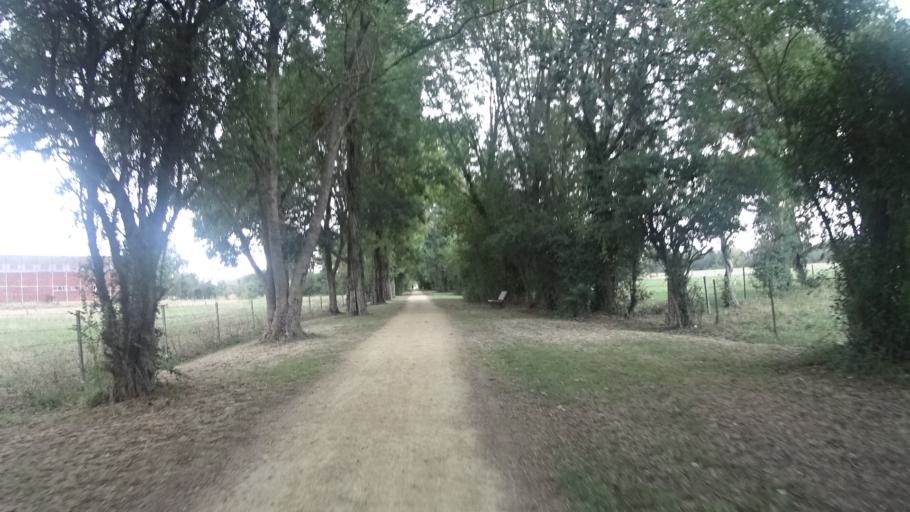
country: FR
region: Picardie
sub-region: Departement de l'Aisne
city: Origny-Sainte-Benoite
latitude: 49.8433
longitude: 3.4896
